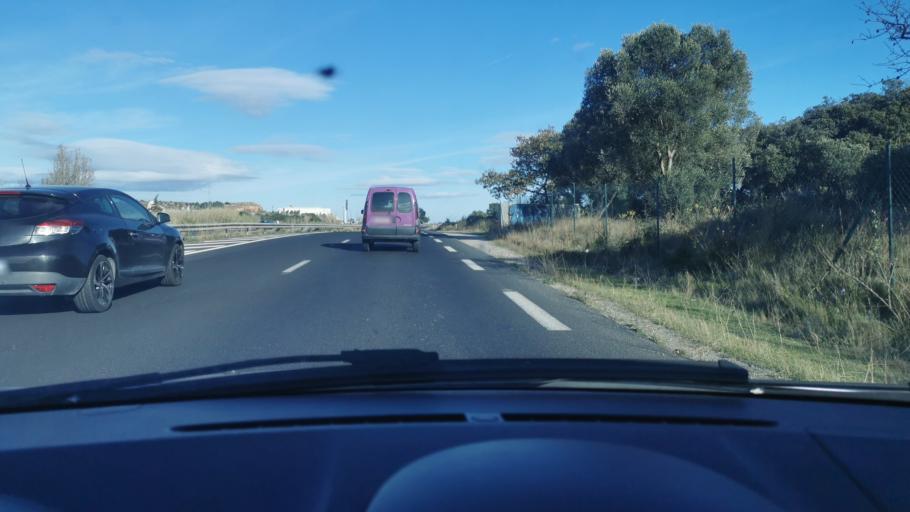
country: FR
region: Languedoc-Roussillon
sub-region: Departement de l'Herault
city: Mireval
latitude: 43.5205
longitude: 3.8107
